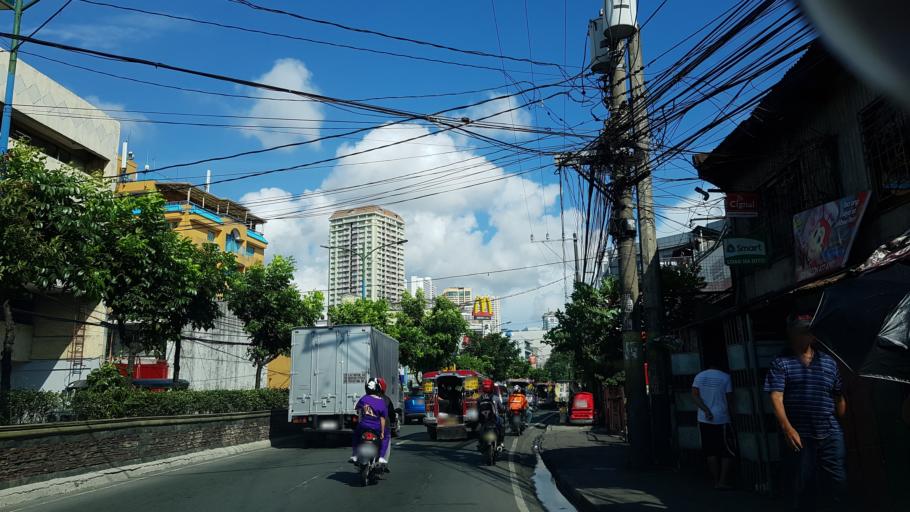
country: PH
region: Metro Manila
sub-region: Mandaluyong
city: Mandaluyong City
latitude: 14.5765
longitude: 121.0398
